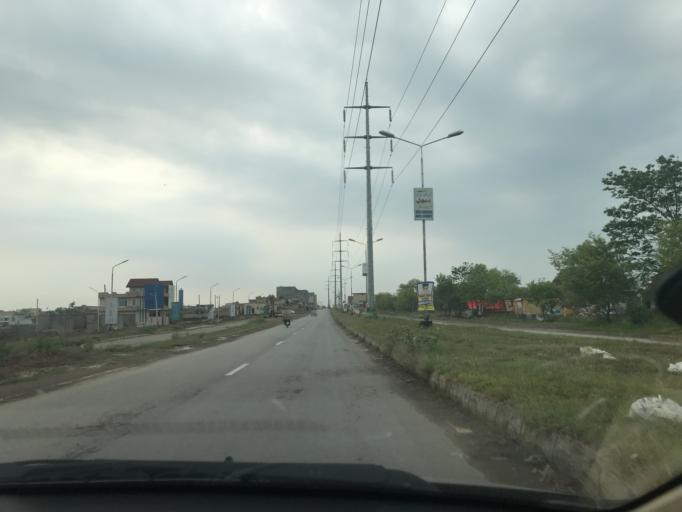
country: PK
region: Islamabad
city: Islamabad
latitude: 33.6881
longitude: 73.1683
